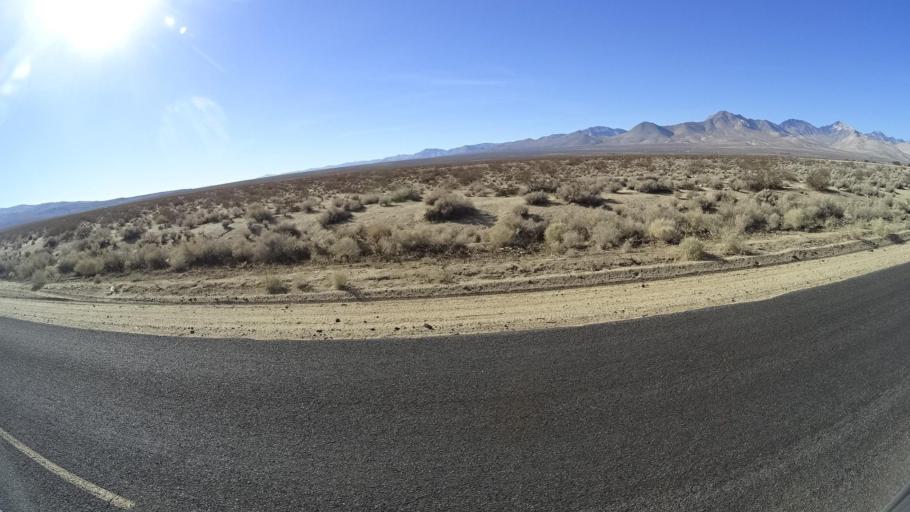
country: US
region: California
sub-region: Kern County
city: Inyokern
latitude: 35.6141
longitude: -117.8026
